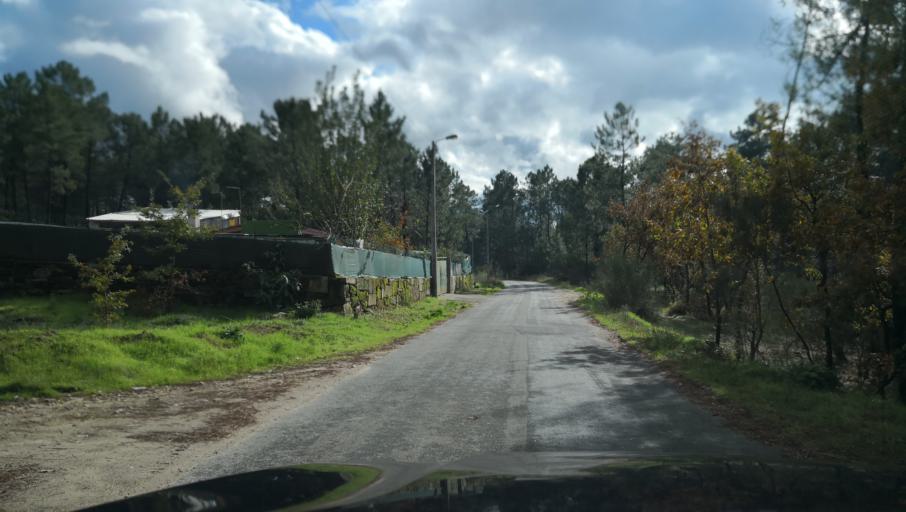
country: PT
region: Vila Real
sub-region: Vila Real
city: Vila Real
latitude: 41.3195
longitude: -7.7537
